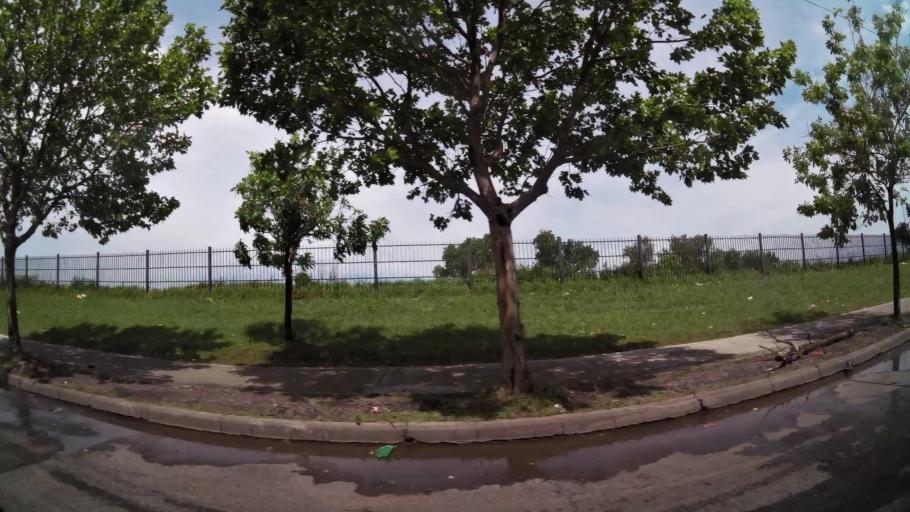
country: AR
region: Buenos Aires F.D.
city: Villa Lugano
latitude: -34.6587
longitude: -58.4624
